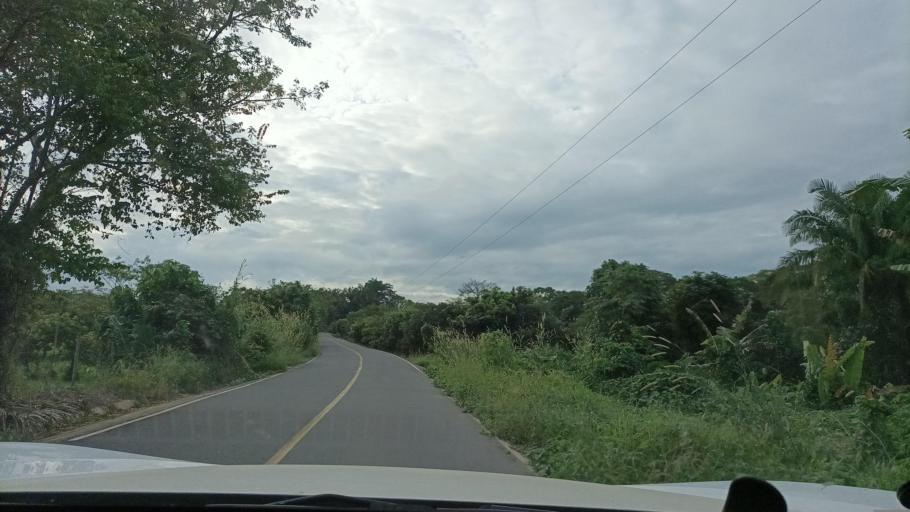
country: MX
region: Veracruz
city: Hidalgotitlan
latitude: 17.7513
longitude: -94.4971
